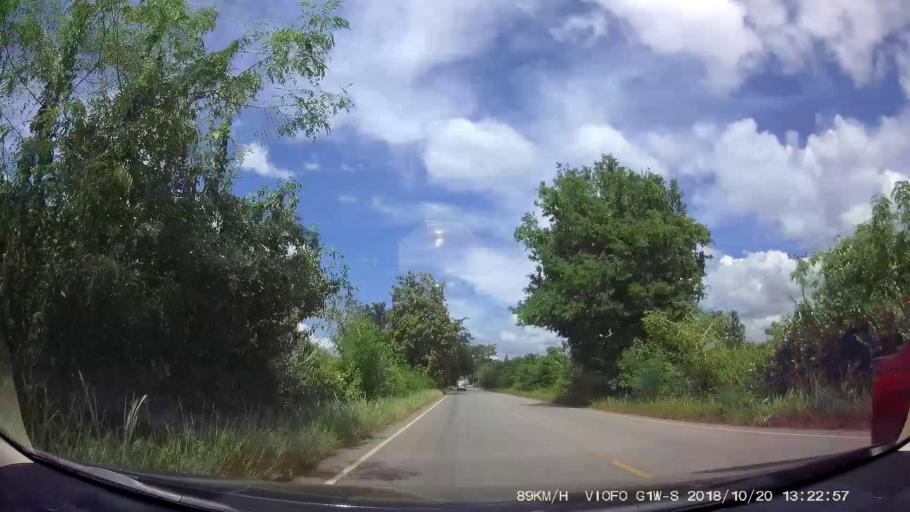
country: TH
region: Chaiyaphum
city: Khon San
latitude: 16.5780
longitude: 101.9188
